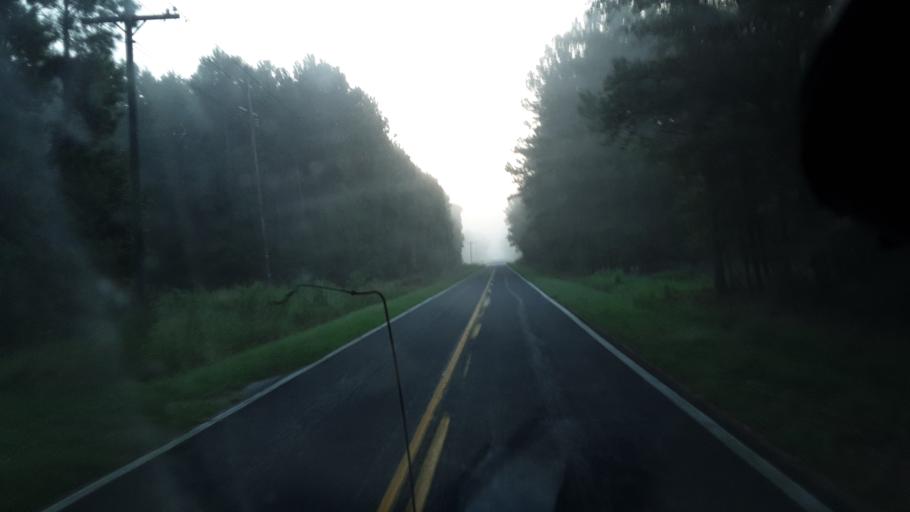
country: US
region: South Carolina
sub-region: Clarendon County
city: Manning
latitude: 33.7202
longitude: -80.1300
